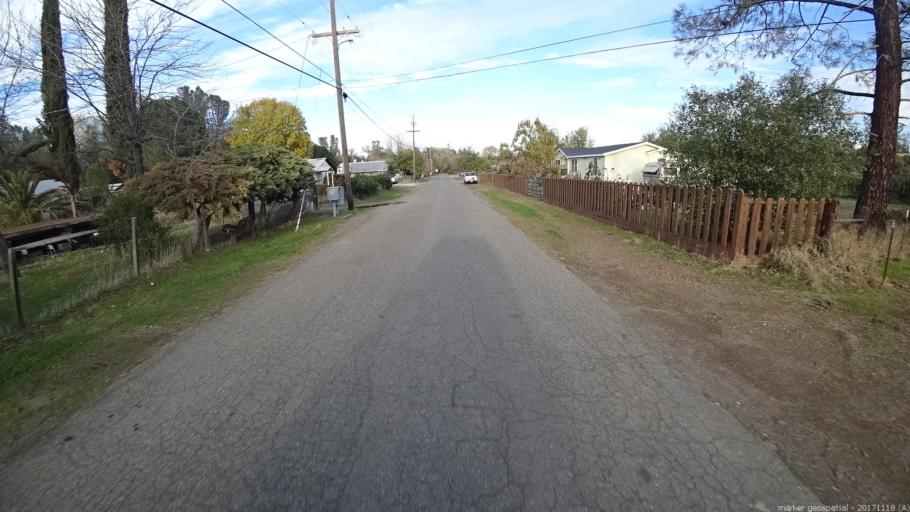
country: US
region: California
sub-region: Shasta County
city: Anderson
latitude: 40.4632
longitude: -122.3311
